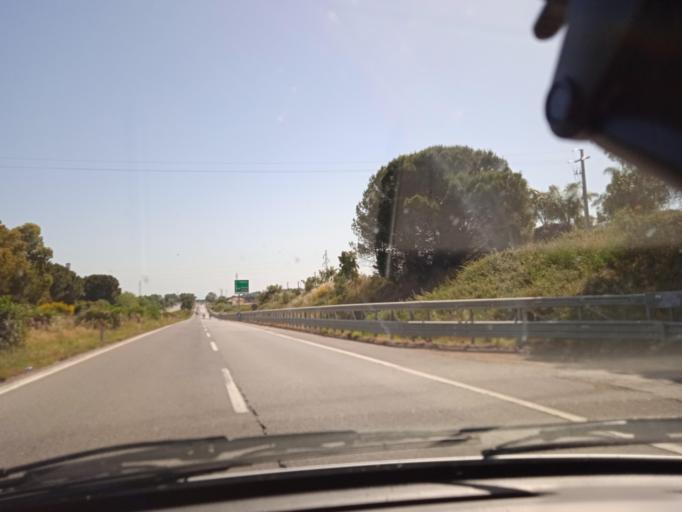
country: IT
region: Sicily
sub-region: Messina
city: San Filippo del Mela
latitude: 38.1873
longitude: 15.2647
